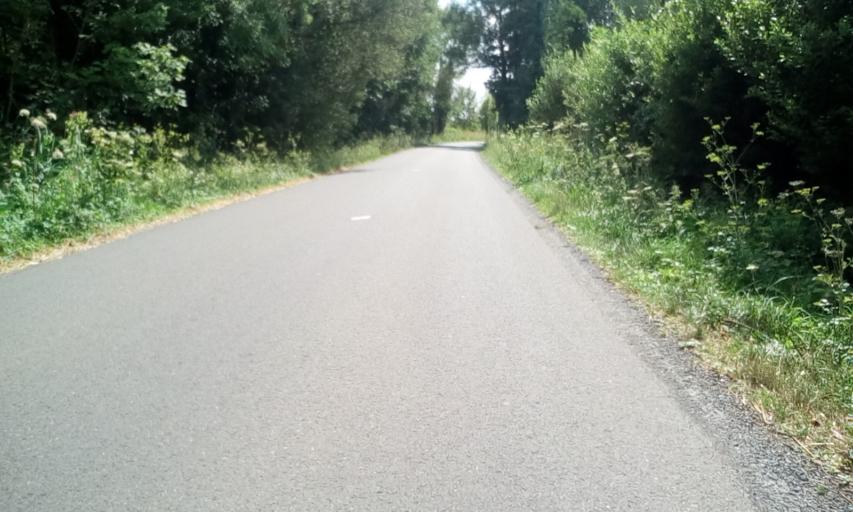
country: FR
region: Lower Normandy
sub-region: Departement du Calvados
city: Bellengreville
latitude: 49.1159
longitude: -0.2236
